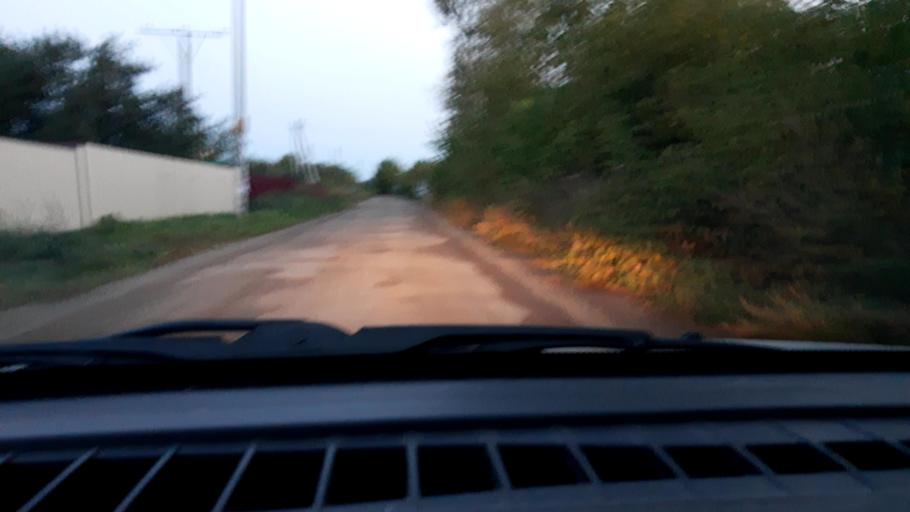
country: RU
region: Nizjnij Novgorod
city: Gorbatovka
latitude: 56.2589
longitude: 43.8282
